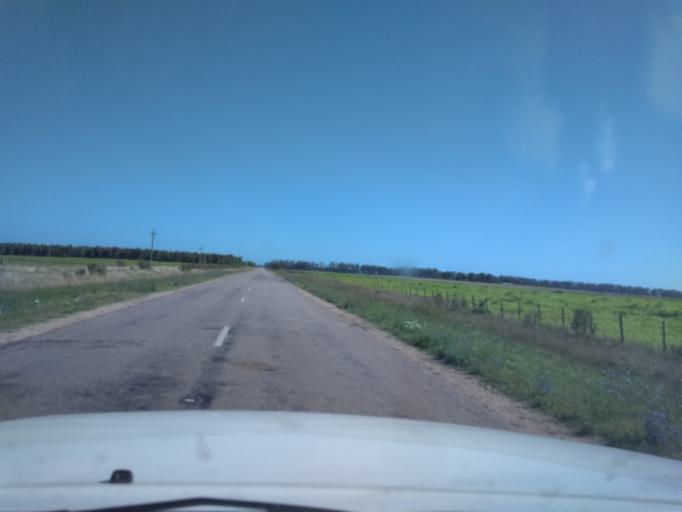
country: UY
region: Canelones
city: San Ramon
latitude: -34.1527
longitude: -55.9463
